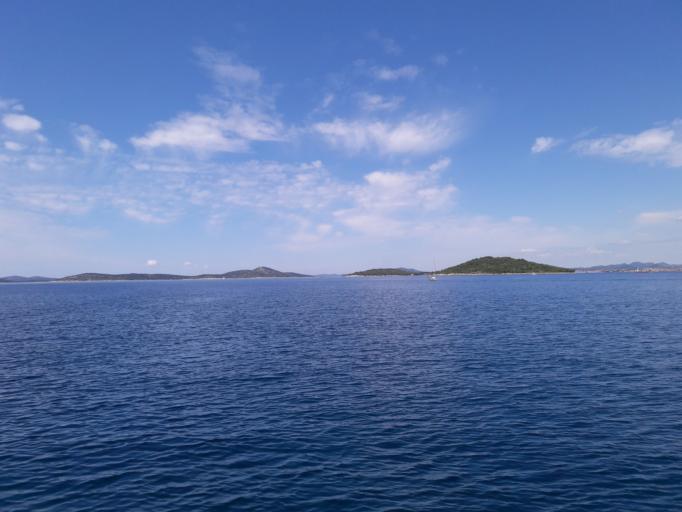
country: HR
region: Sibensko-Kniniska
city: Vodice
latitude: 43.7025
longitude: 15.8300
